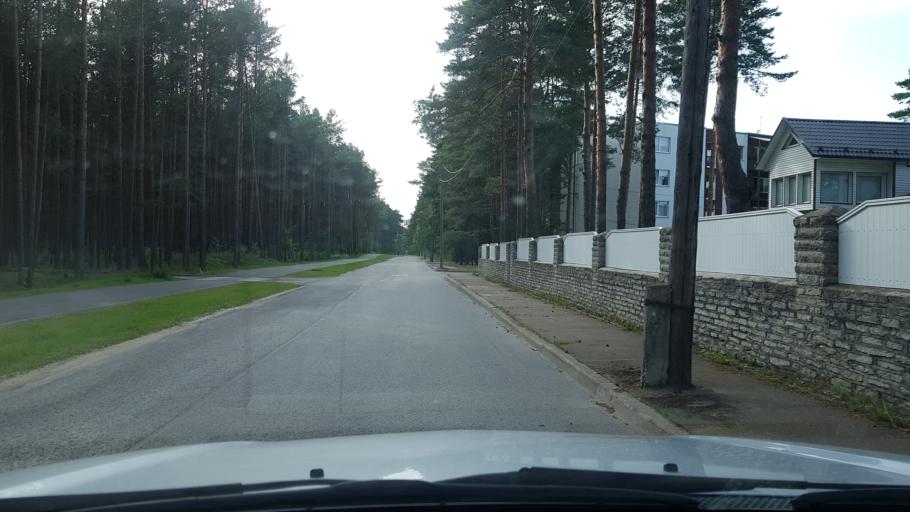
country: EE
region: Ida-Virumaa
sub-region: Narva-Joesuu linn
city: Narva-Joesuu
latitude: 59.4553
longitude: 28.0458
